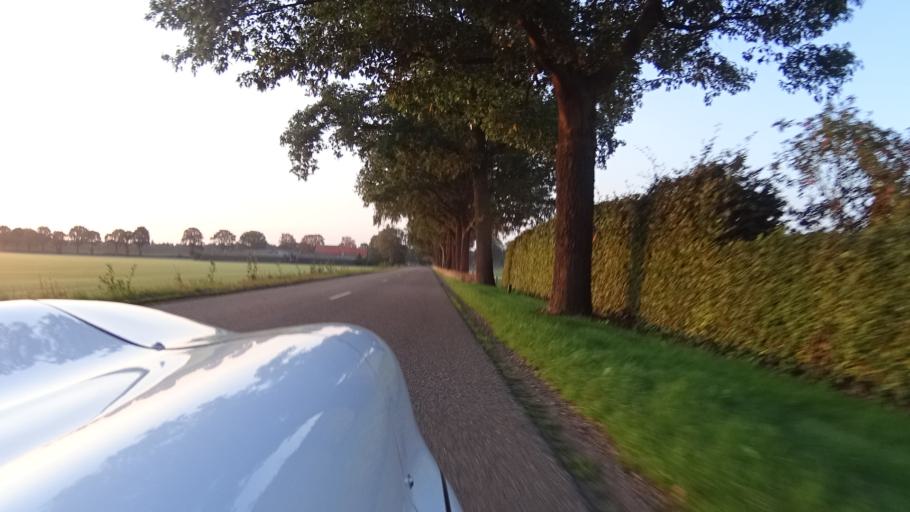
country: NL
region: North Brabant
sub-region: Gemeente Mill en Sint Hubert
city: Wilbertoord
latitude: 51.5980
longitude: 5.7917
